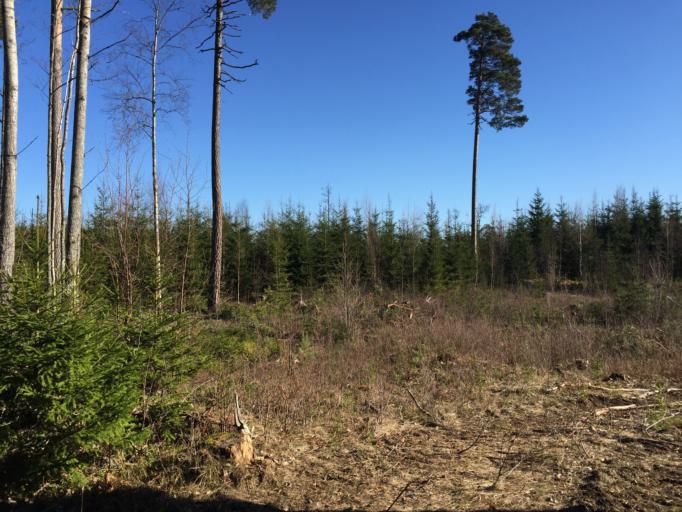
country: SE
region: Soedermanland
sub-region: Vingakers Kommun
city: Vingaker
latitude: 59.0082
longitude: 15.6758
